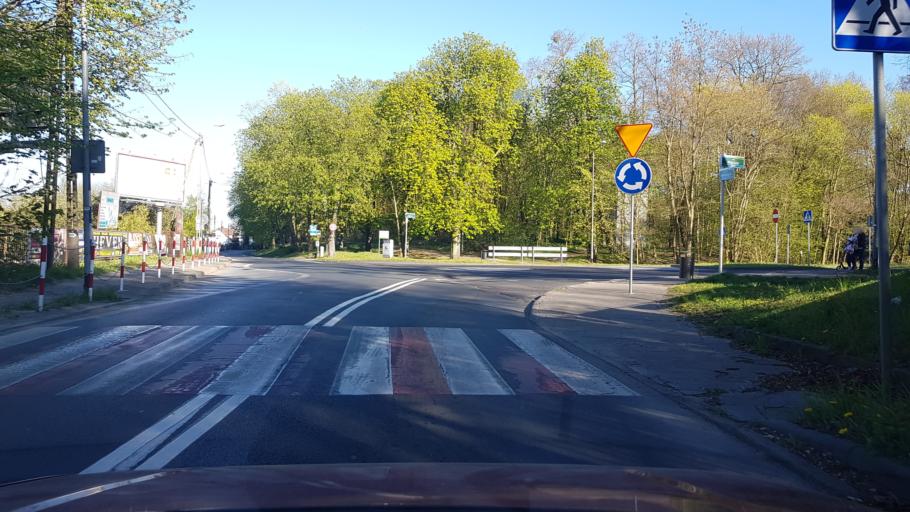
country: PL
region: West Pomeranian Voivodeship
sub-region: Szczecin
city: Szczecin
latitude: 53.3745
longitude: 14.6438
